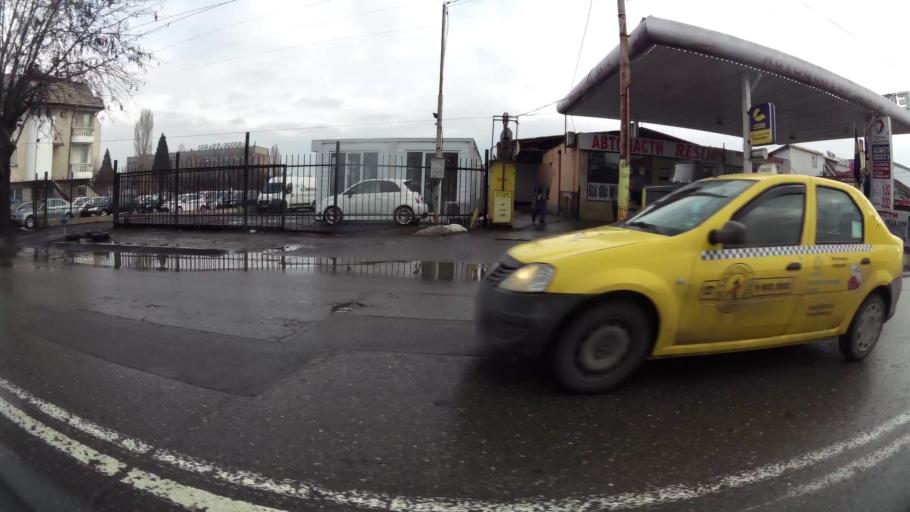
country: BG
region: Sofiya
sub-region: Obshtina Bozhurishte
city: Bozhurishte
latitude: 42.7312
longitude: 23.2542
